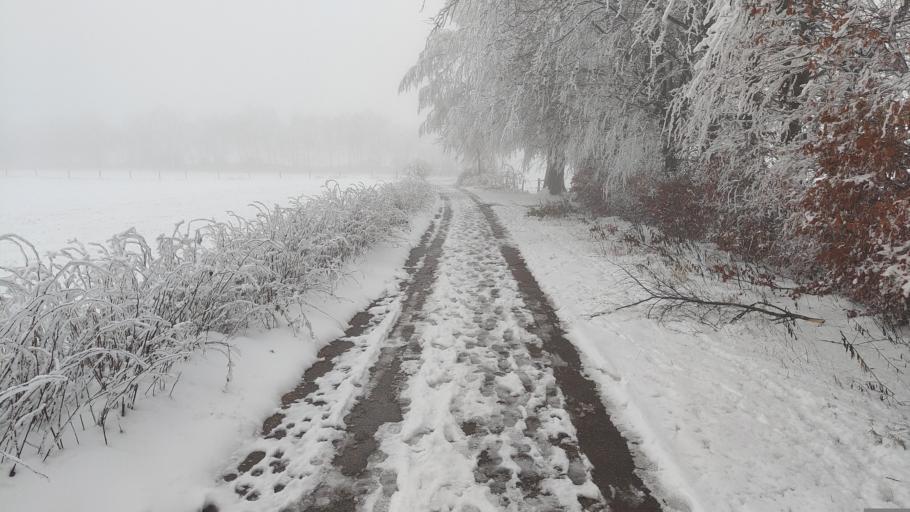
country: DE
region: North Rhine-Westphalia
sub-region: Regierungsbezirk Koln
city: Monschau
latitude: 50.5747
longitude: 6.2098
